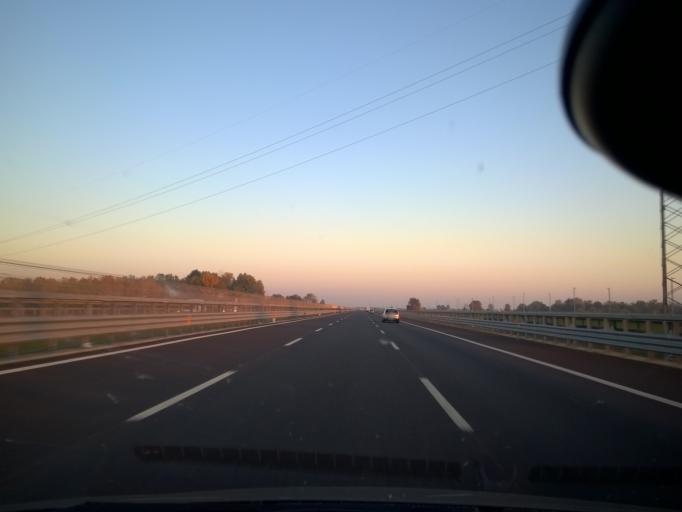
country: IT
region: Lombardy
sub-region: Provincia di Bergamo
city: Bariano
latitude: 45.4964
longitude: 9.7209
